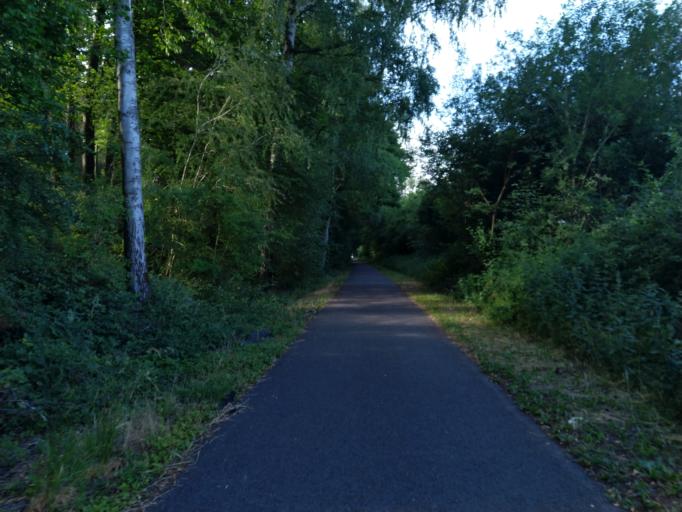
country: BE
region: Wallonia
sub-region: Province du Hainaut
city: Erquelinnes
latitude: 50.3313
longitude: 4.0987
